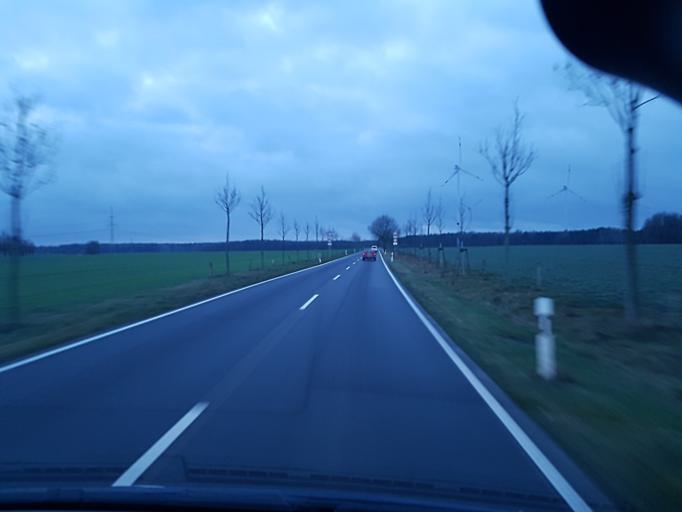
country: DE
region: Brandenburg
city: Sallgast
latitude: 51.6342
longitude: 13.8506
